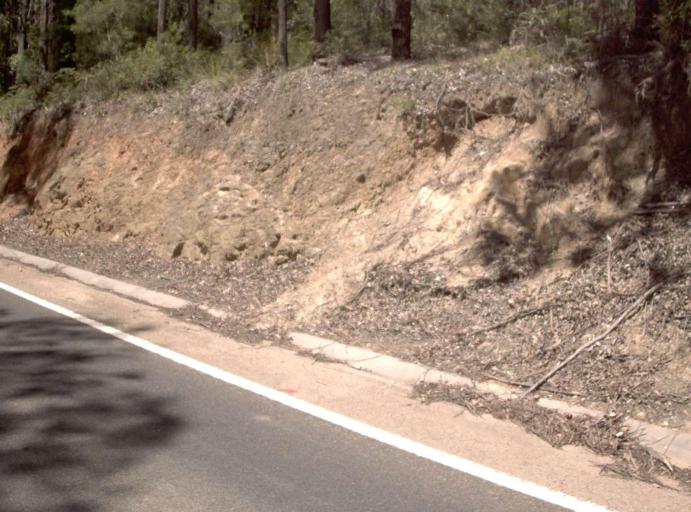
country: AU
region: New South Wales
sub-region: Bombala
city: Bombala
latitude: -37.6019
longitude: 148.9058
